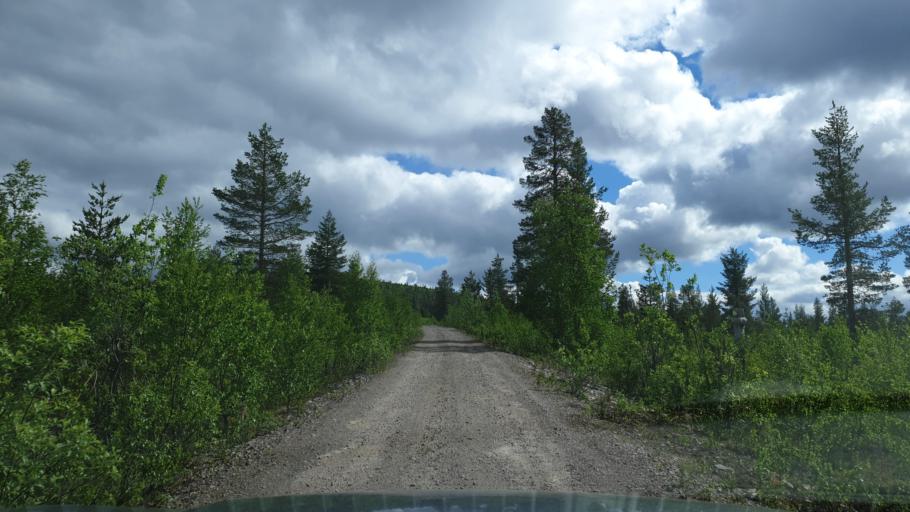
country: SE
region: Norrbotten
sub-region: Jokkmokks Kommun
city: Jokkmokk
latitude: 67.0317
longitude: 19.9974
